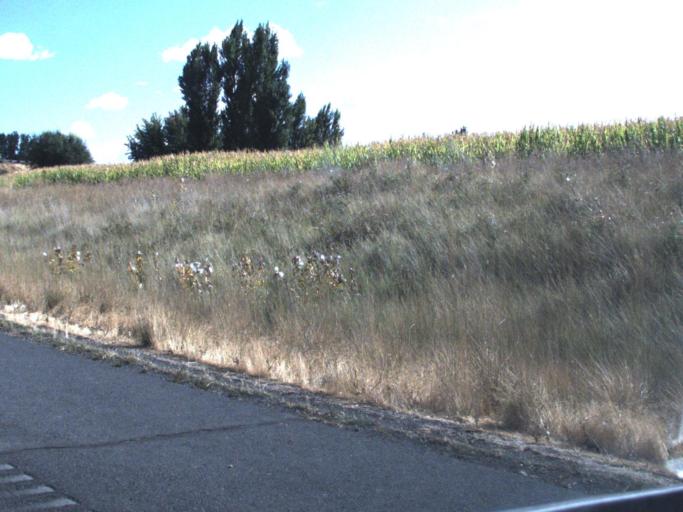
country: US
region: Washington
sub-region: Yakima County
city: Grandview
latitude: 46.2641
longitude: -119.8958
